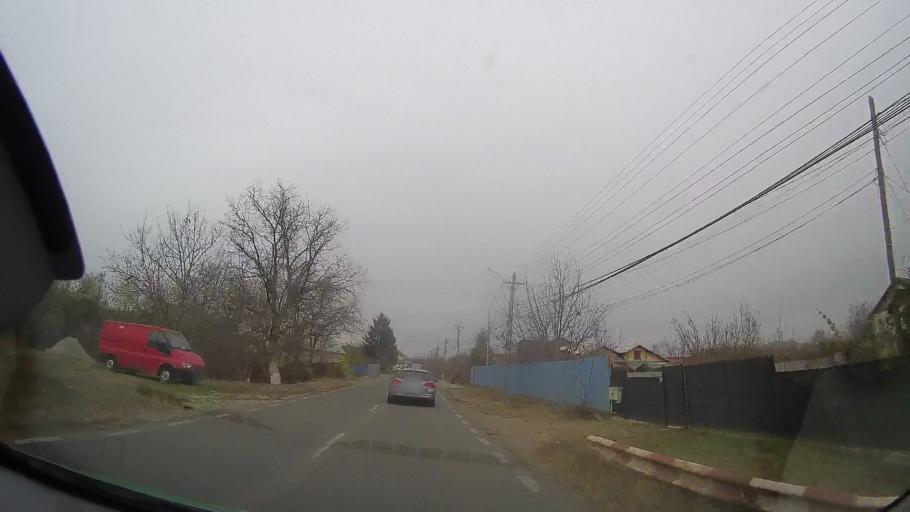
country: RO
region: Prahova
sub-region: Oras Baicoi
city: Liliesti
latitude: 45.0290
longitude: 25.8868
